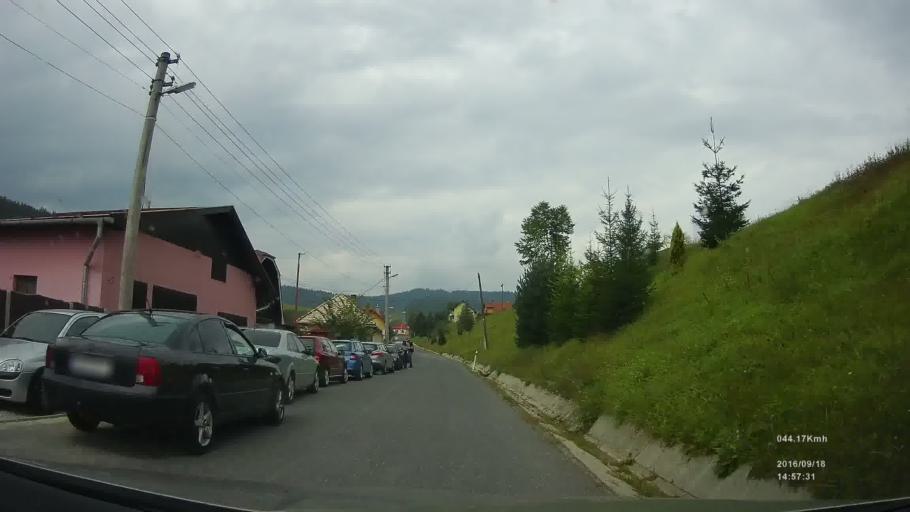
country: SK
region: Presovsky
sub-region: Okres Presov
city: Levoca
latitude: 49.0225
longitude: 20.5242
